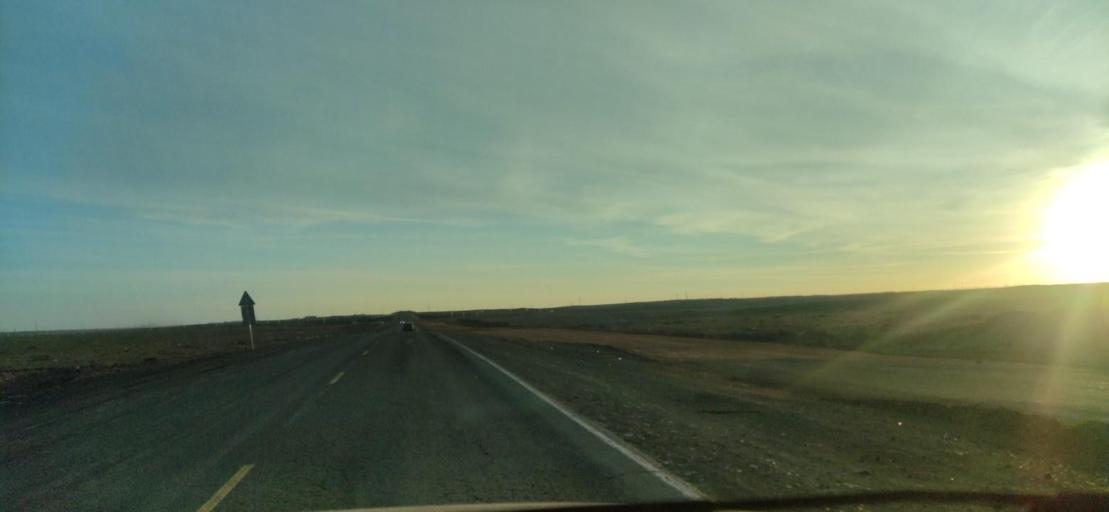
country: KZ
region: Qaraghandy
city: Saryshaghan
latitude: 46.0467
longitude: 73.5949
